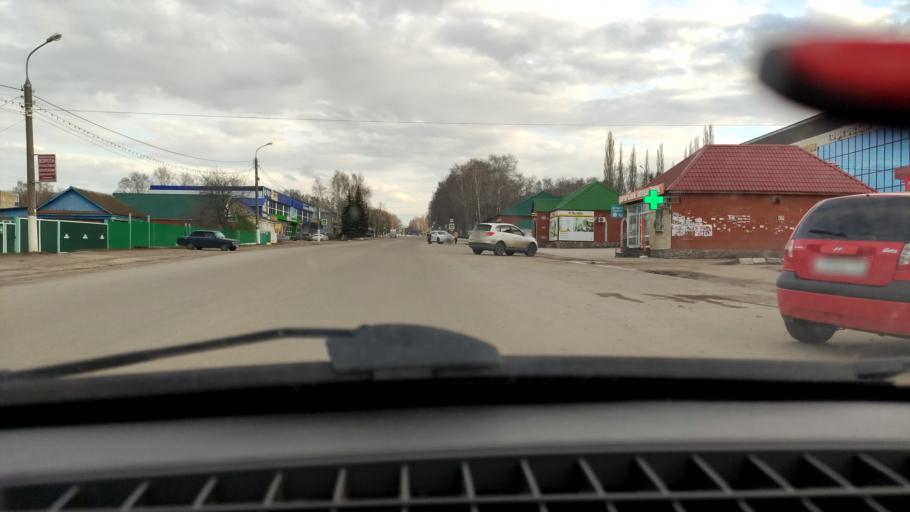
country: RU
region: Bashkortostan
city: Tolbazy
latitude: 54.0182
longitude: 55.8864
